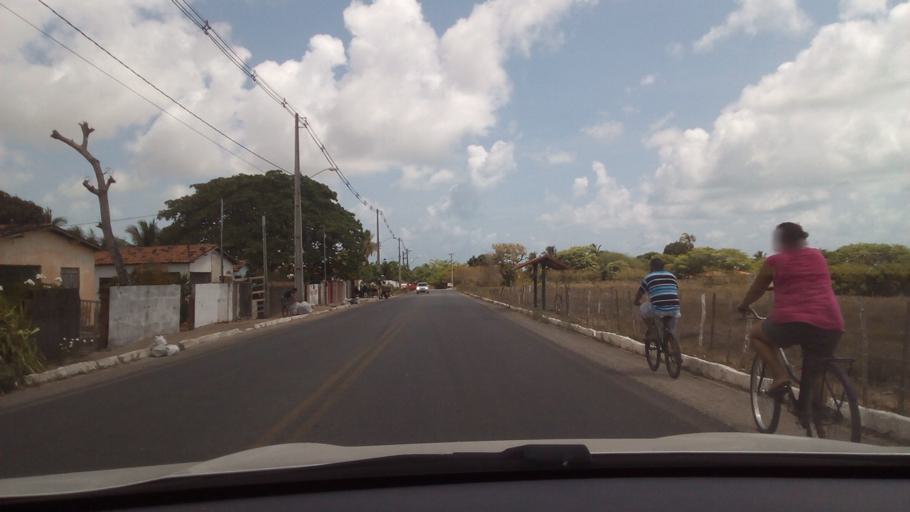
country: BR
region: Paraiba
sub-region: Conde
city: Conde
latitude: -7.2071
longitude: -34.8269
